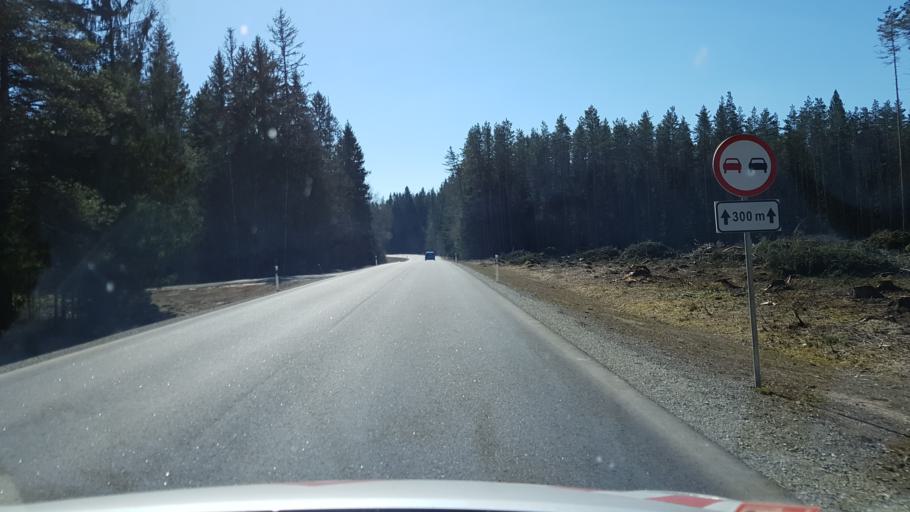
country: EE
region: Laeaene-Virumaa
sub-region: Vinni vald
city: Vinni
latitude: 59.1372
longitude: 26.5981
